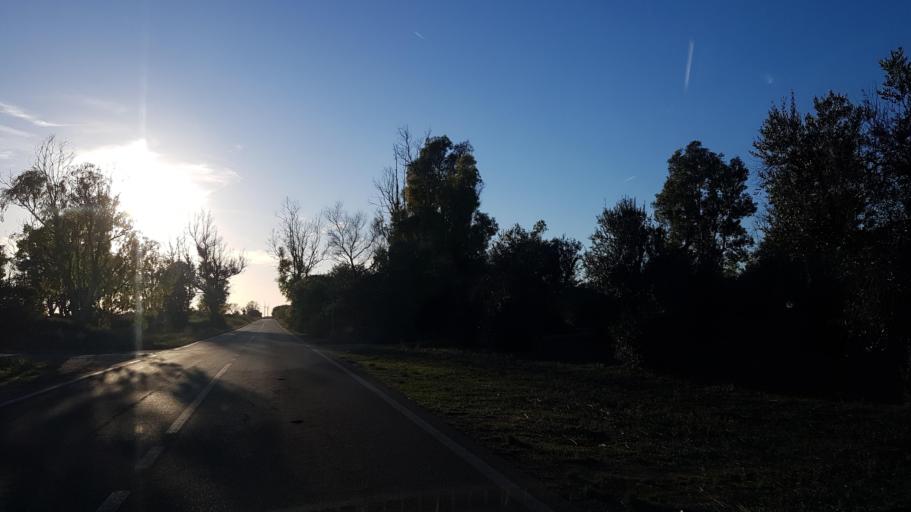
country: IT
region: Apulia
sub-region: Provincia di Lecce
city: Giorgilorio
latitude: 40.4191
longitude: 18.2187
